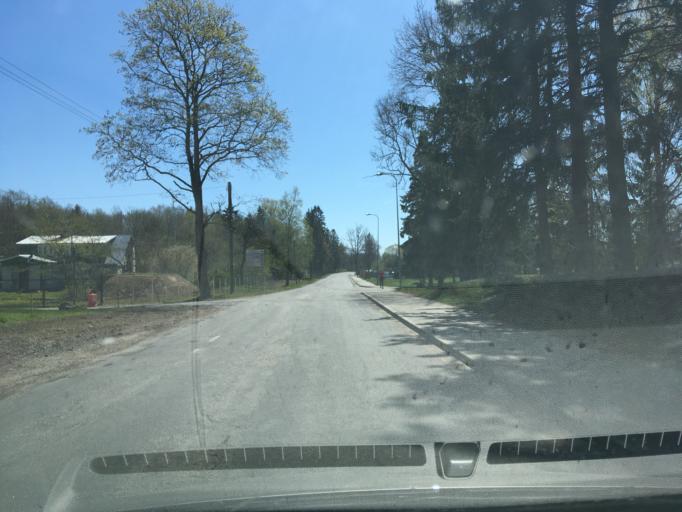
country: EE
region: Harju
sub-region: Raasiku vald
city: Arukula
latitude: 59.3664
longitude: 25.0816
